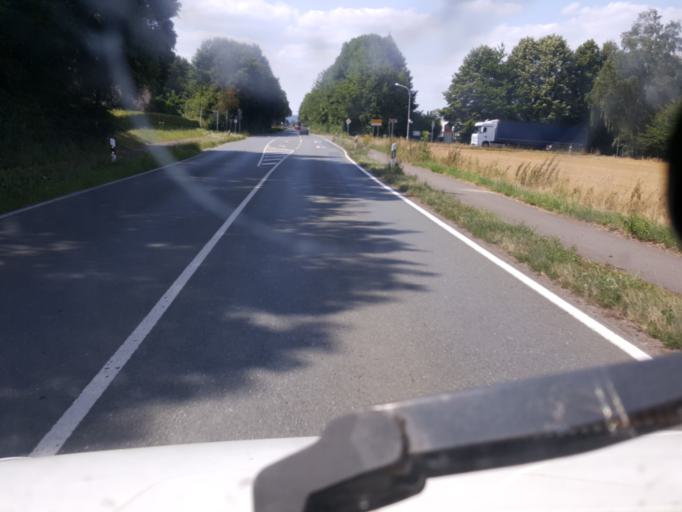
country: DE
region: North Rhine-Westphalia
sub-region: Regierungsbezirk Detmold
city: Minden
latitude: 52.2630
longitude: 8.8511
